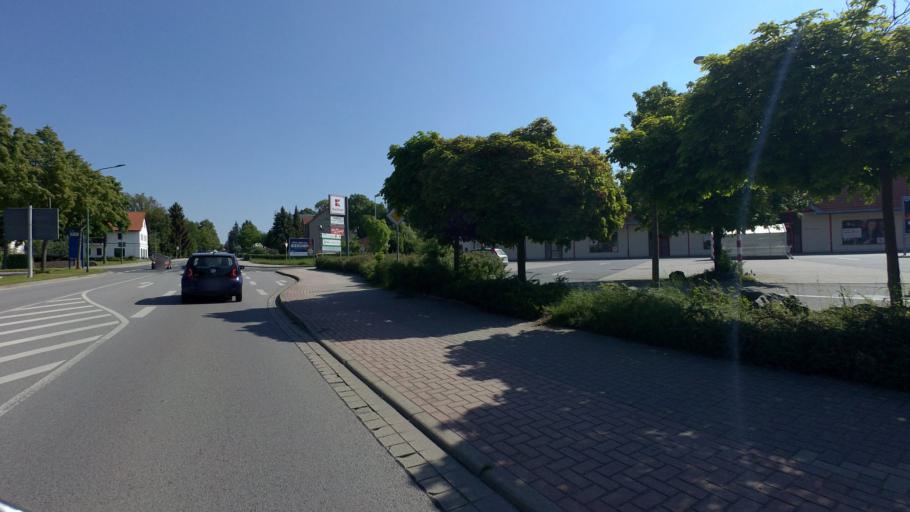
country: DE
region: Saxony
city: Neustadt in Sachsen
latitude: 51.0285
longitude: 14.2177
